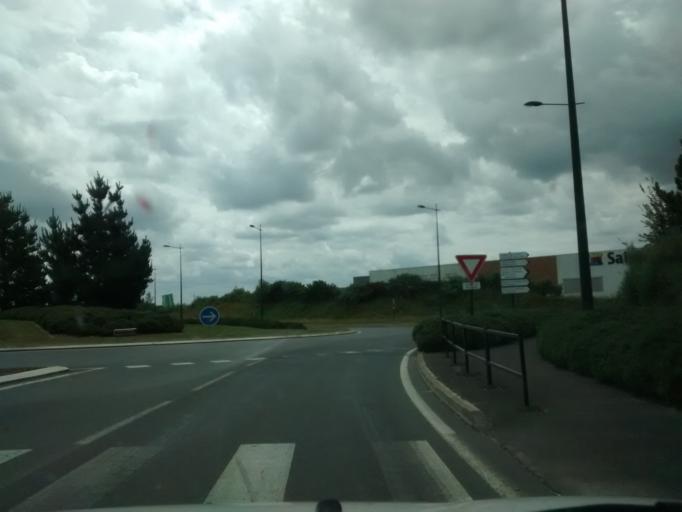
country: FR
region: Brittany
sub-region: Departement des Cotes-d'Armor
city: Lannion
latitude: 48.7516
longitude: -3.4492
